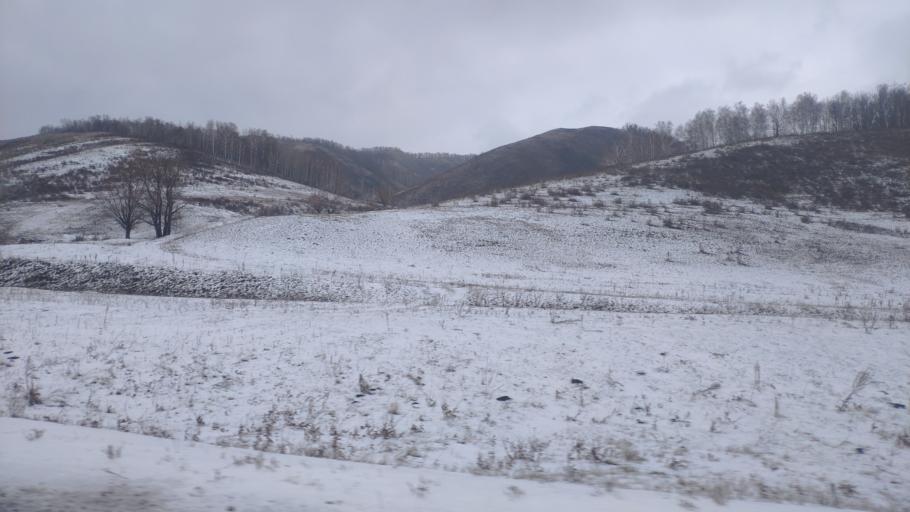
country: RU
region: Bashkortostan
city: Isyangulovo
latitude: 52.1618
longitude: 56.9072
